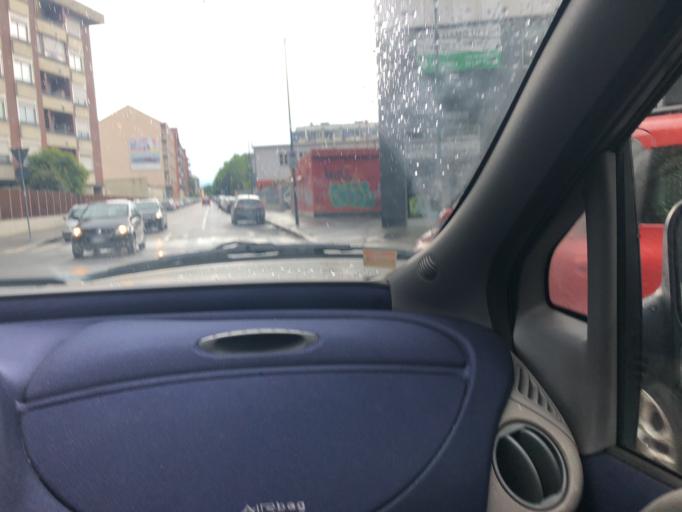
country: IT
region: Piedmont
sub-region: Provincia di Torino
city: Lesna
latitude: 45.0769
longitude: 7.6255
